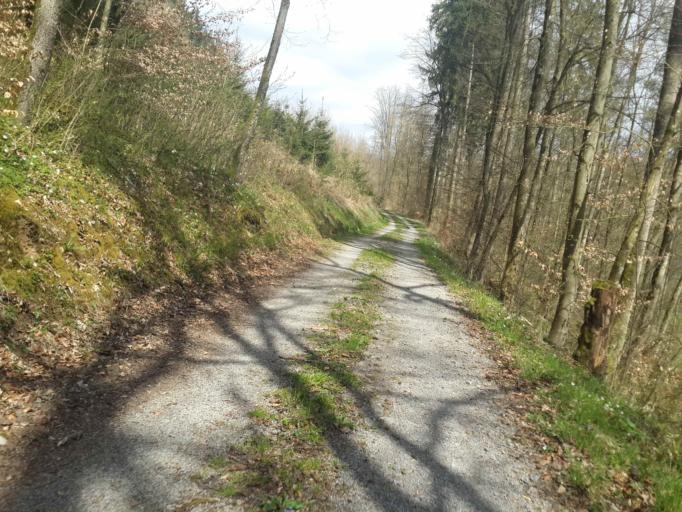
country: DE
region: Baden-Wuerttemberg
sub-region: Regierungsbezirk Stuttgart
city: Neudenau
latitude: 49.2947
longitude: 9.2472
